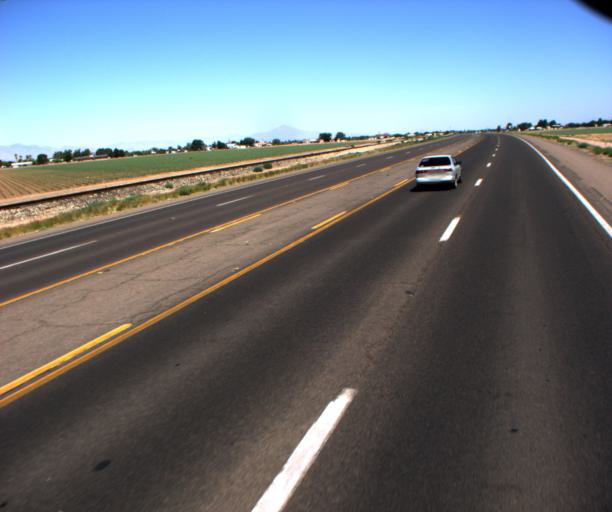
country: US
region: Arizona
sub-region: Graham County
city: Pima
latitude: 32.8805
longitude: -109.8065
